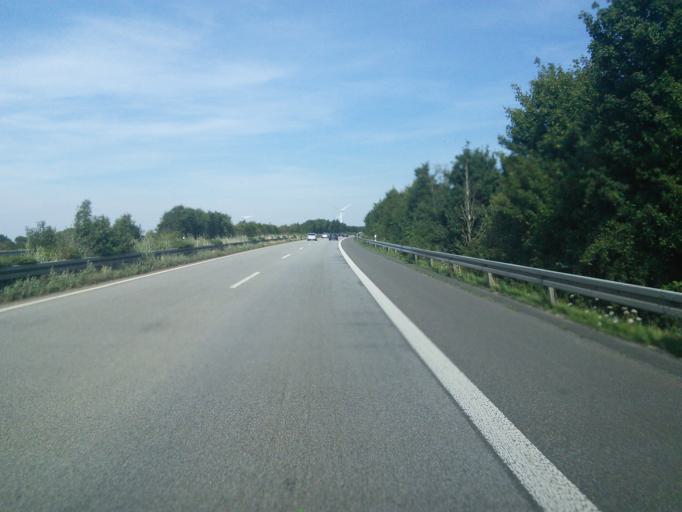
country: DE
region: North Rhine-Westphalia
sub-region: Regierungsbezirk Dusseldorf
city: Schwalmtal
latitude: 51.2056
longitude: 6.3086
